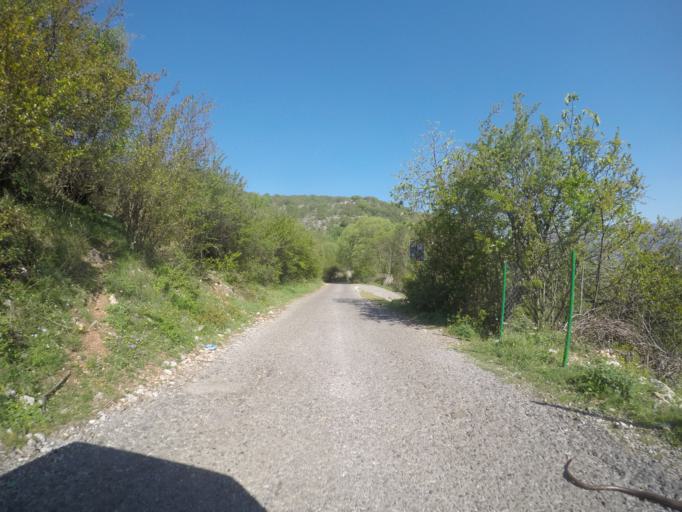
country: ME
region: Danilovgrad
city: Danilovgrad
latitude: 42.5334
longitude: 19.0895
